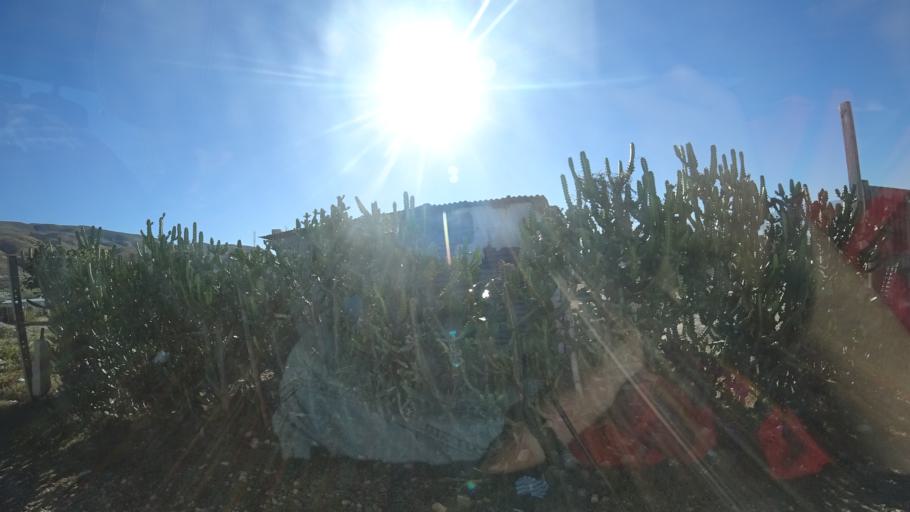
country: HT
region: Ouest
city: Cabaret
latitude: 18.6897
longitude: -72.3185
